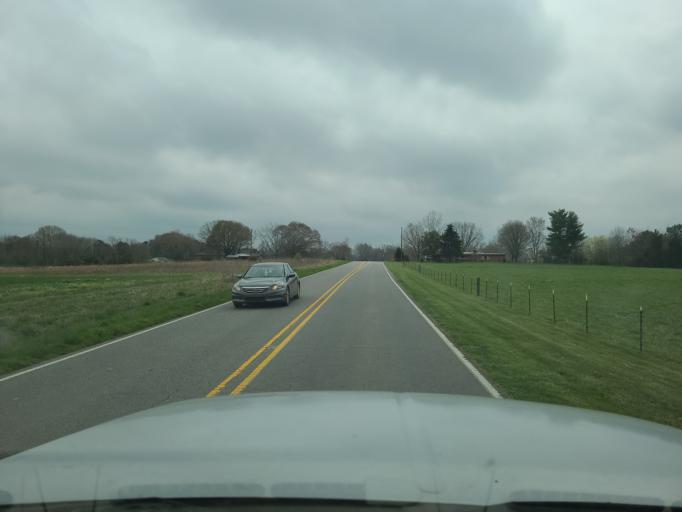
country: US
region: North Carolina
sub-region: Cleveland County
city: Shelby
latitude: 35.3902
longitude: -81.6241
